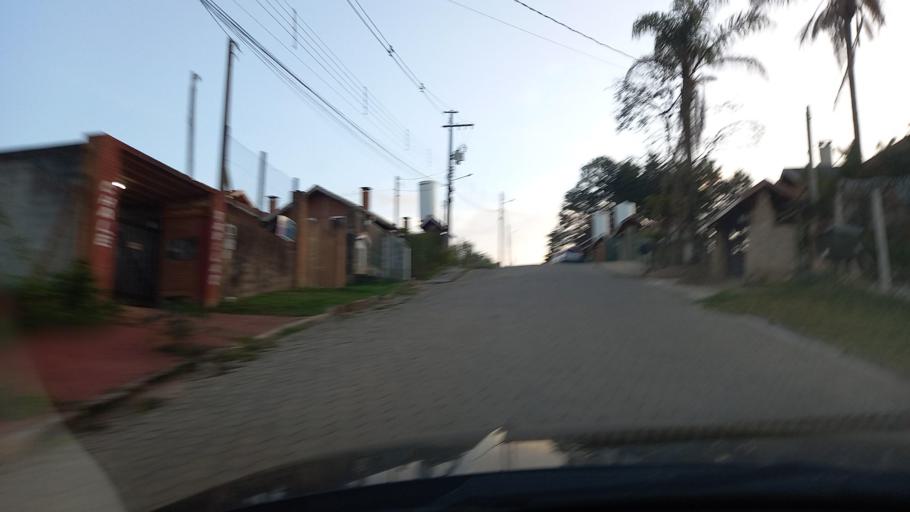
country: BR
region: Minas Gerais
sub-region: Camanducaia
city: Camanducaia
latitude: -22.8575
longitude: -46.0319
